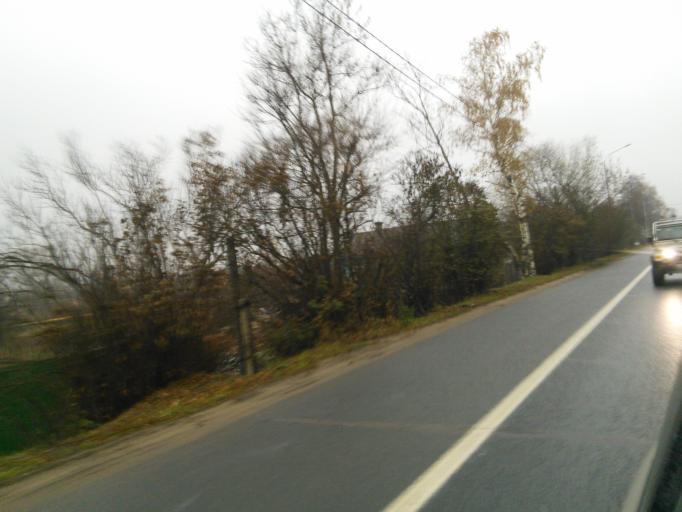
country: RU
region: Jaroslavl
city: Petrovsk
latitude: 57.0086
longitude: 39.2587
